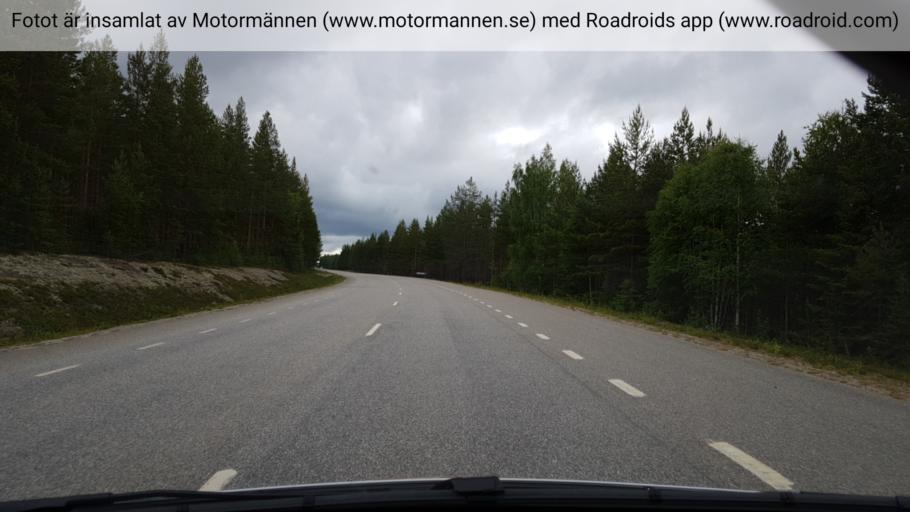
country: SE
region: Vaesterbotten
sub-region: Norsjo Kommun
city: Norsjoe
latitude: 64.5883
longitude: 19.2964
